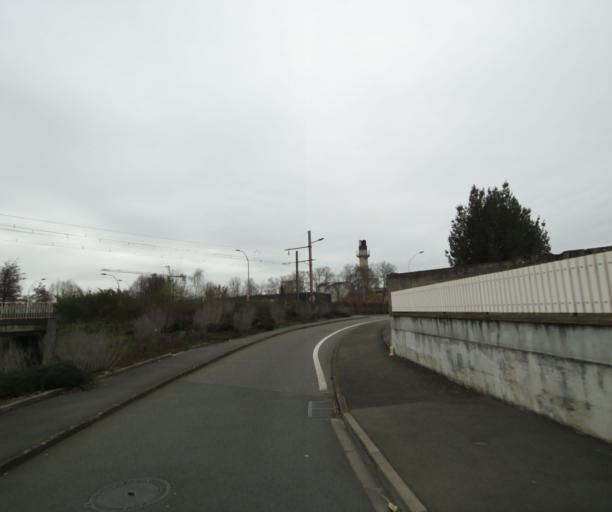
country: FR
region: Pays de la Loire
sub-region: Departement de la Sarthe
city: Sarge-les-le-Mans
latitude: 47.9987
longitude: 0.2360
